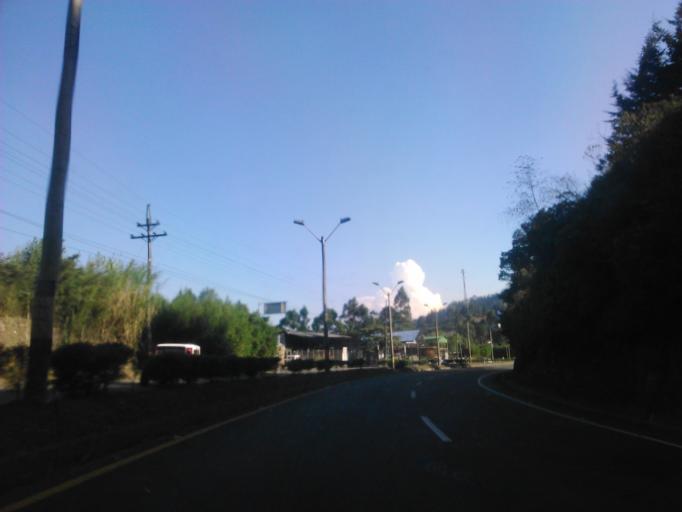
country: CO
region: Antioquia
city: Guarne
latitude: 6.2898
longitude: -75.4490
